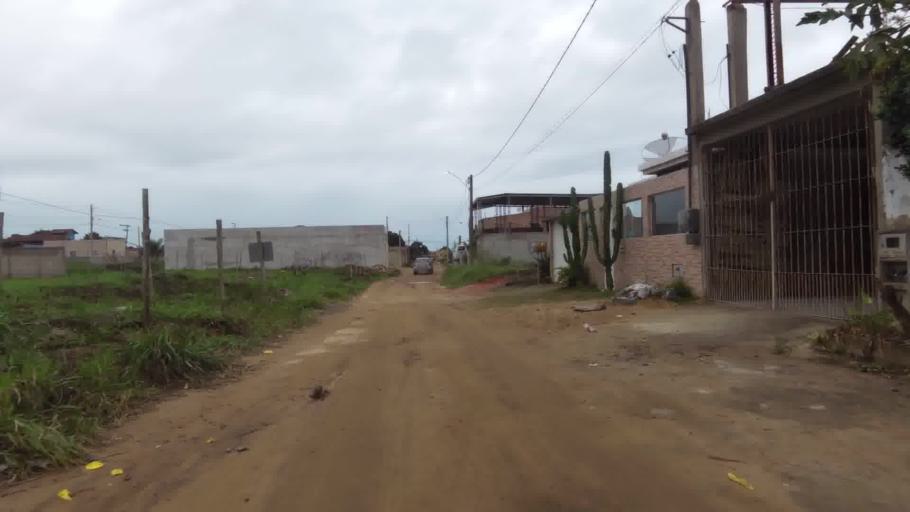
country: BR
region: Espirito Santo
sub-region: Marataizes
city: Marataizes
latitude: -21.0486
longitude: -40.8402
